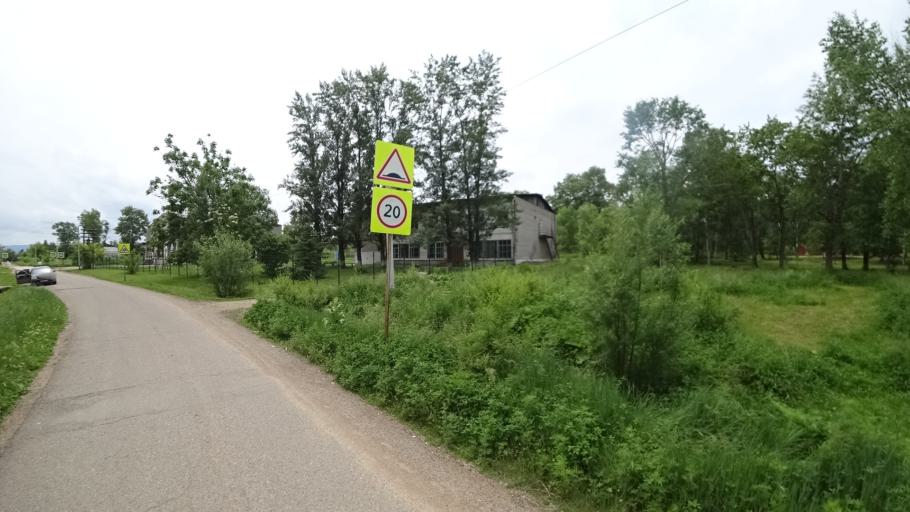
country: RU
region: Primorskiy
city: Novosysoyevka
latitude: 44.2396
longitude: 133.3640
